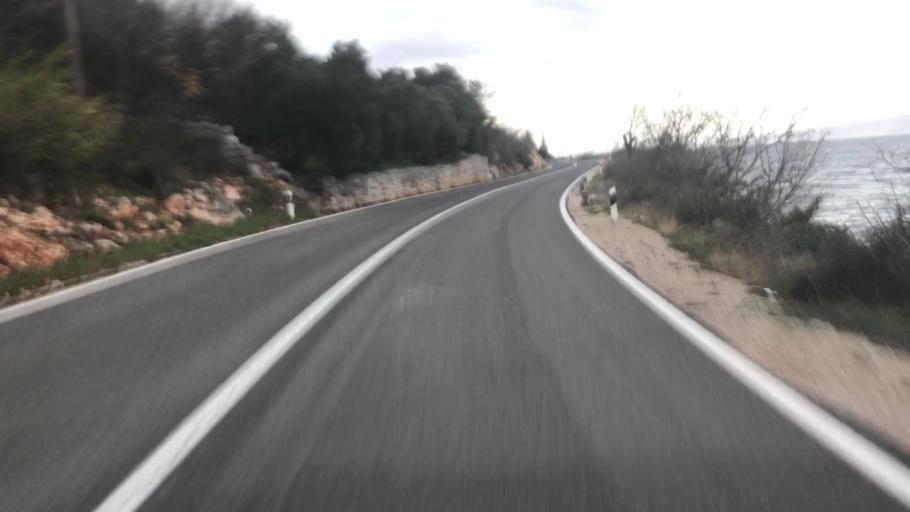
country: HR
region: Zadarska
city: Razanac
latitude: 44.3354
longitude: 15.3511
